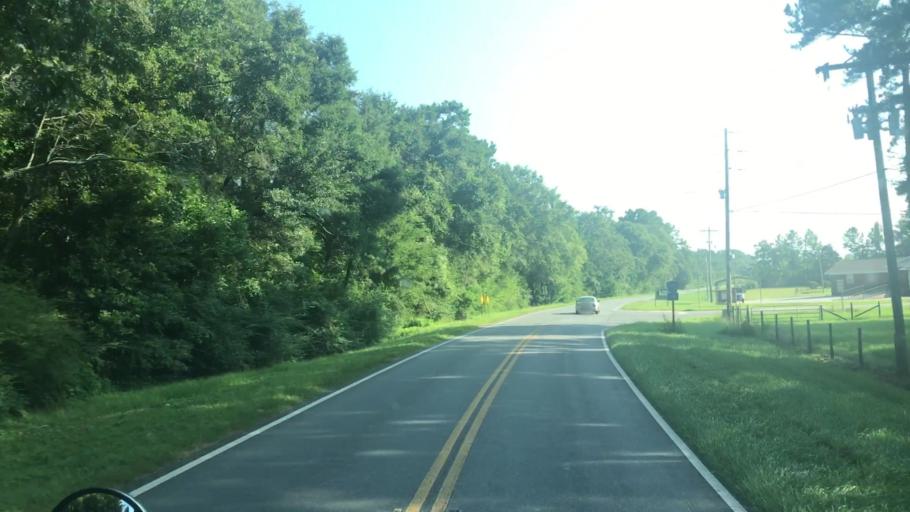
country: US
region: Florida
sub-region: Gadsden County
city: Quincy
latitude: 30.6356
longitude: -84.5770
